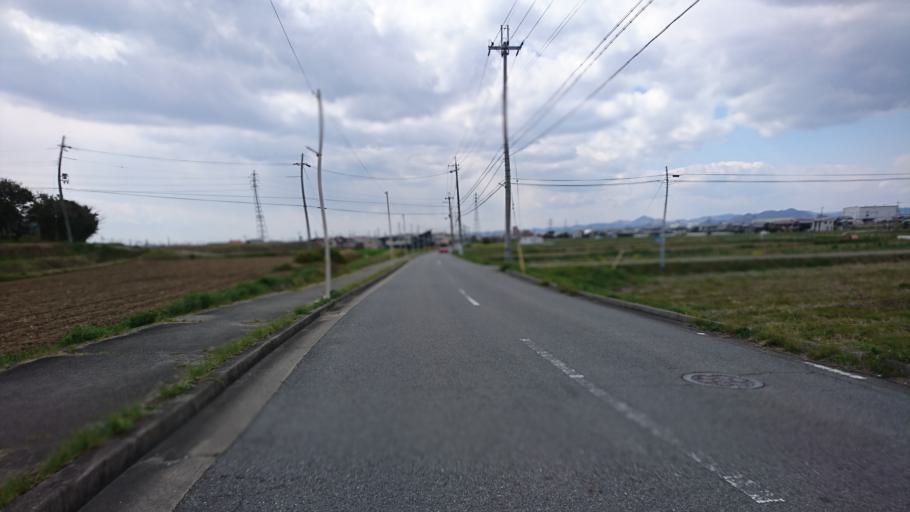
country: JP
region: Hyogo
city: Miki
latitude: 34.7531
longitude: 134.9199
